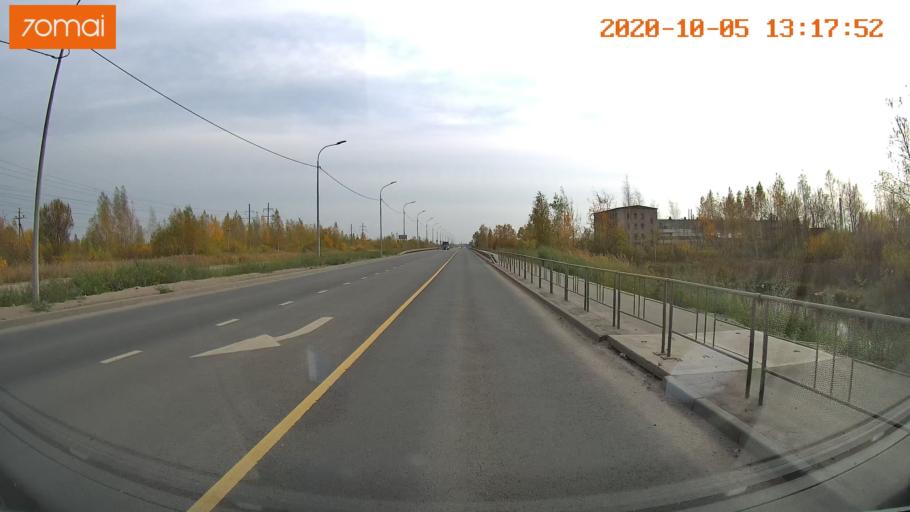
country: RU
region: Ivanovo
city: Novo-Talitsy
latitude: 56.9826
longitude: 40.9140
